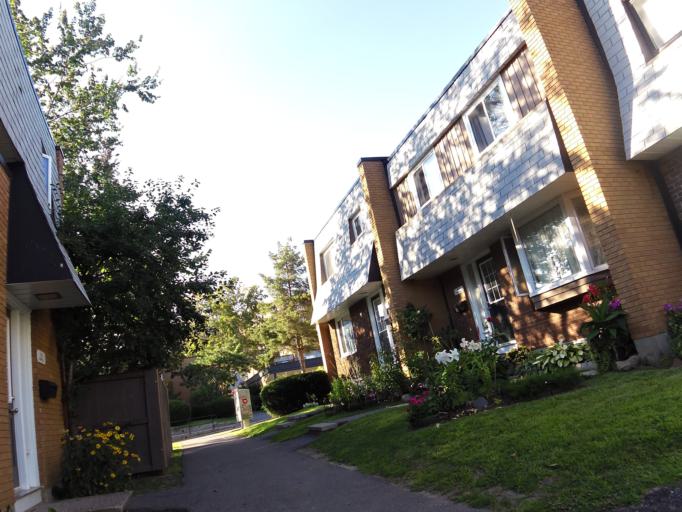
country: CA
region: Ontario
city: Ottawa
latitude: 45.3502
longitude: -75.7282
